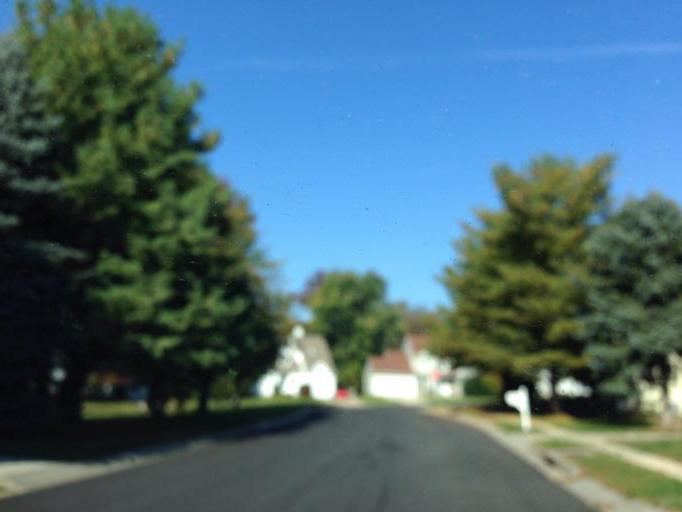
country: US
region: Maryland
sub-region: Howard County
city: Ellicott City
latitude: 39.2731
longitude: -76.8133
